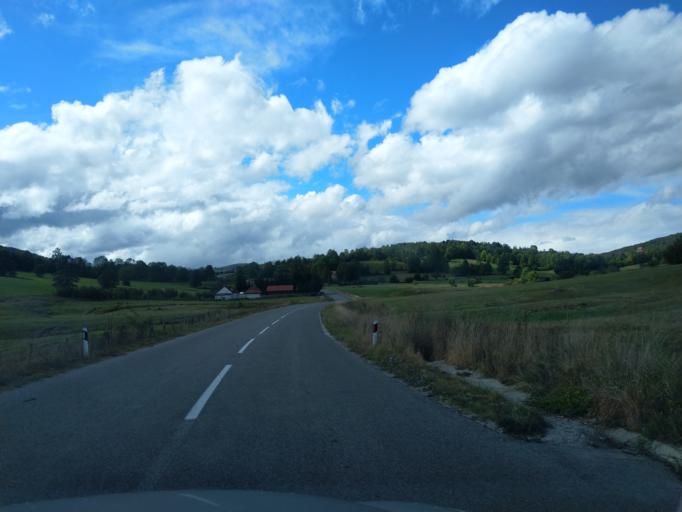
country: RS
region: Central Serbia
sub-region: Zlatiborski Okrug
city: Cajetina
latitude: 43.7219
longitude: 19.8260
